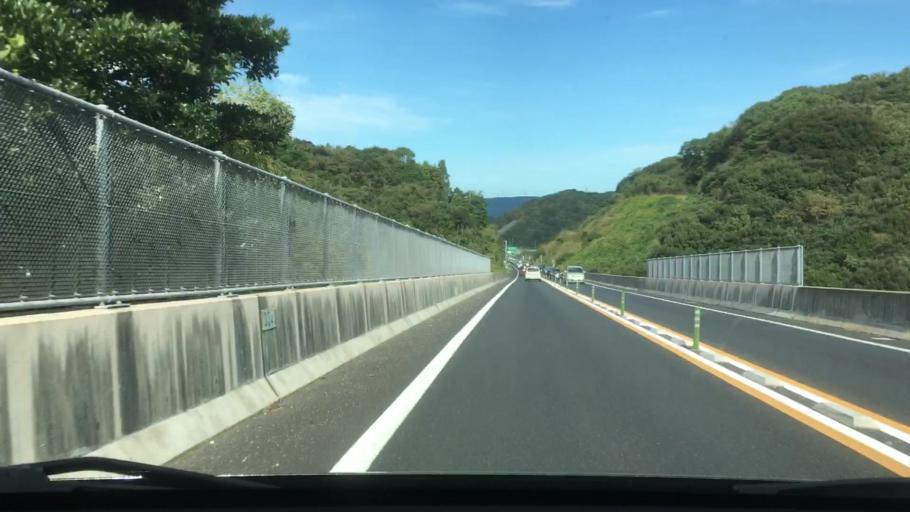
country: JP
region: Nagasaki
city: Sasebo
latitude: 33.1953
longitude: 129.6792
